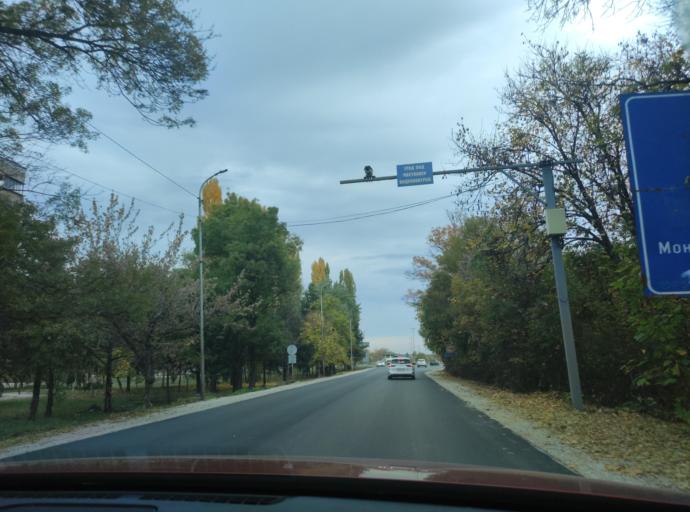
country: BG
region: Montana
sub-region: Obshtina Montana
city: Montana
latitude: 43.4005
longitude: 23.2400
